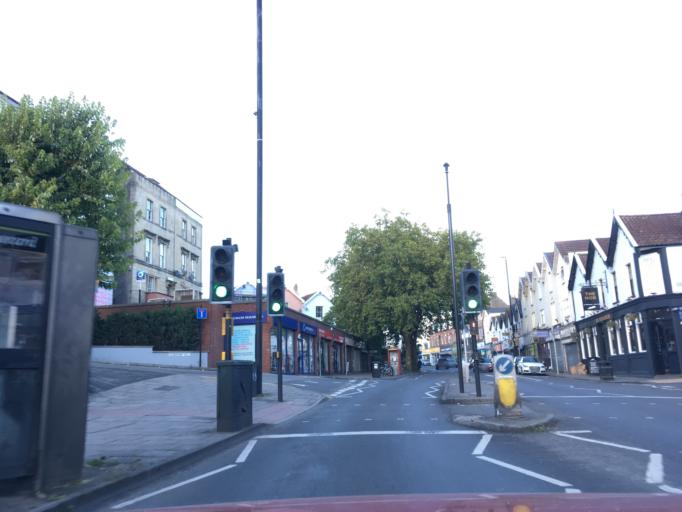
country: GB
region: England
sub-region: Bristol
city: Bristol
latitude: 51.4718
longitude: -2.5923
